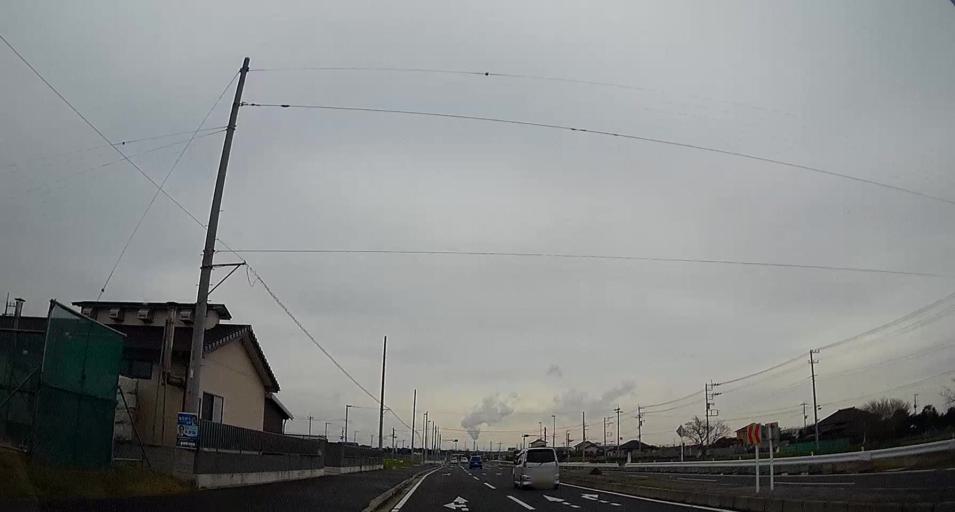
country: JP
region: Chiba
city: Kisarazu
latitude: 35.4252
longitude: 139.9214
